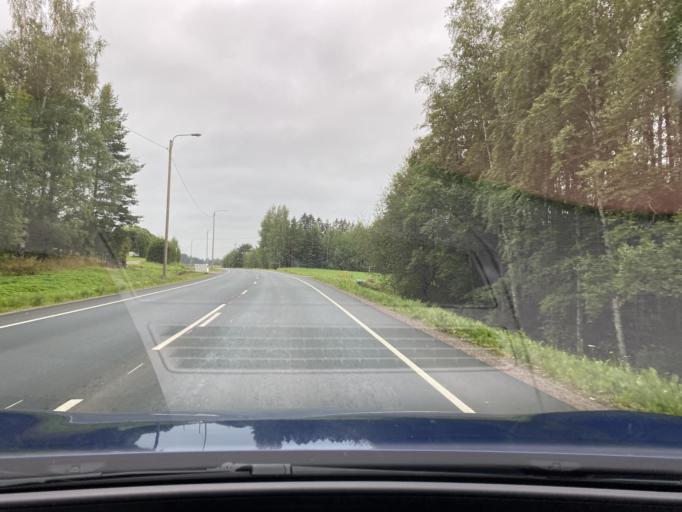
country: FI
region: Kymenlaakso
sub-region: Kouvola
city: Kouvola
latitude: 60.8820
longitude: 26.6010
